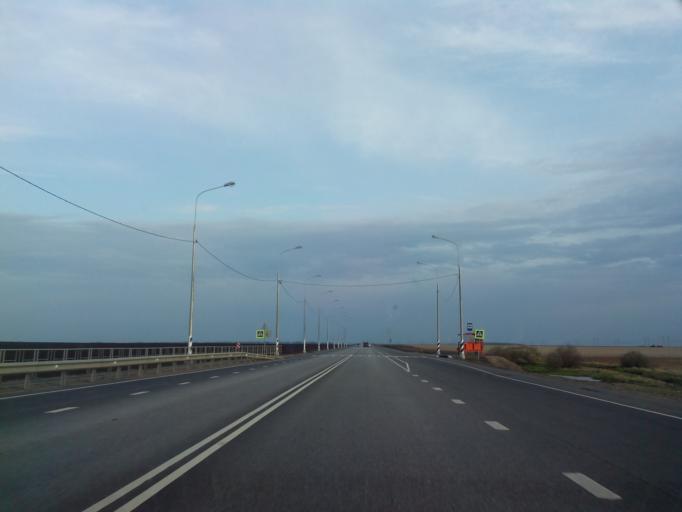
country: RU
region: Rjazan
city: Ryazhsk
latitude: 53.5775
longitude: 40.0439
